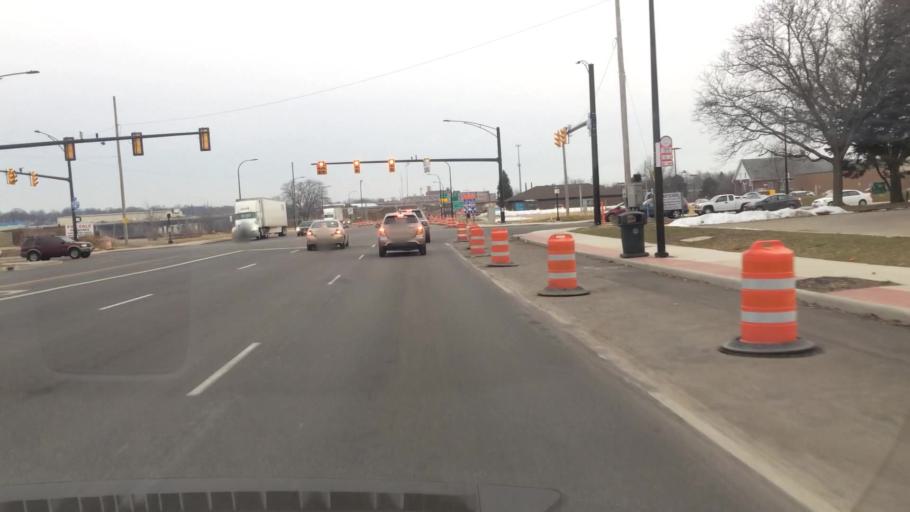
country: US
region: Ohio
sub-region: Summit County
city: Akron
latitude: 41.0666
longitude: -81.5264
